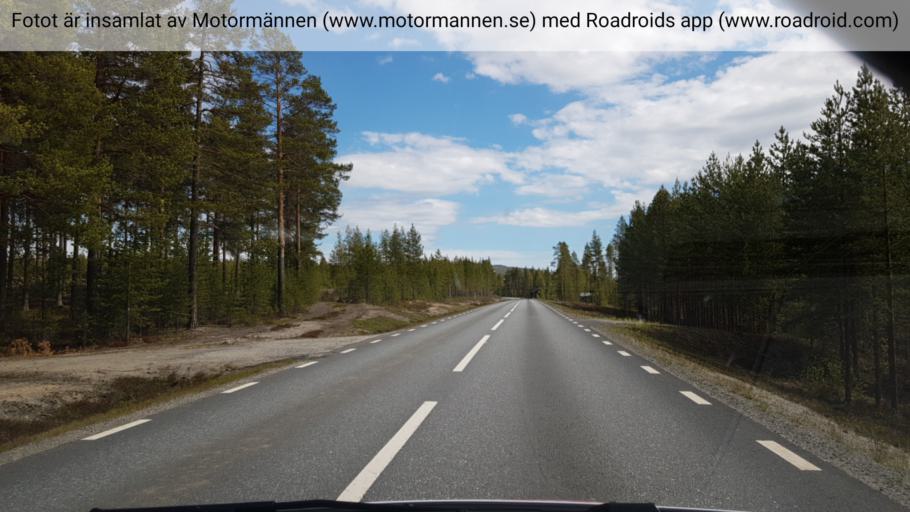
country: SE
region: Vaesterbotten
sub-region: Bjurholms Kommun
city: Bjurholm
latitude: 64.2860
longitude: 19.2090
